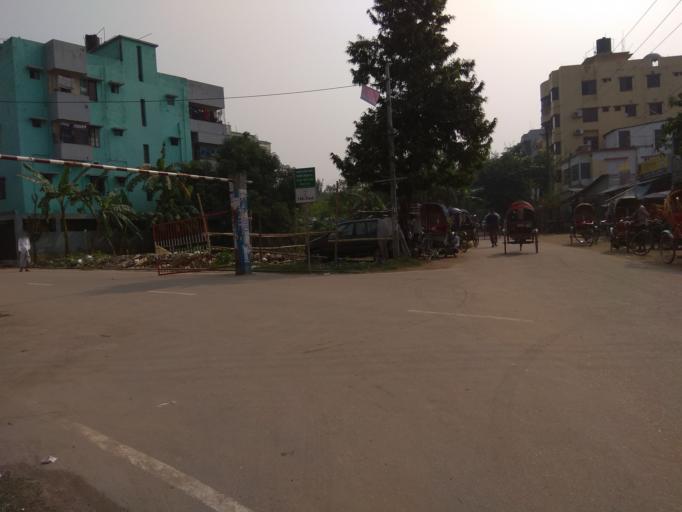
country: BD
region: Dhaka
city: Tungi
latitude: 23.8634
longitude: 90.3865
